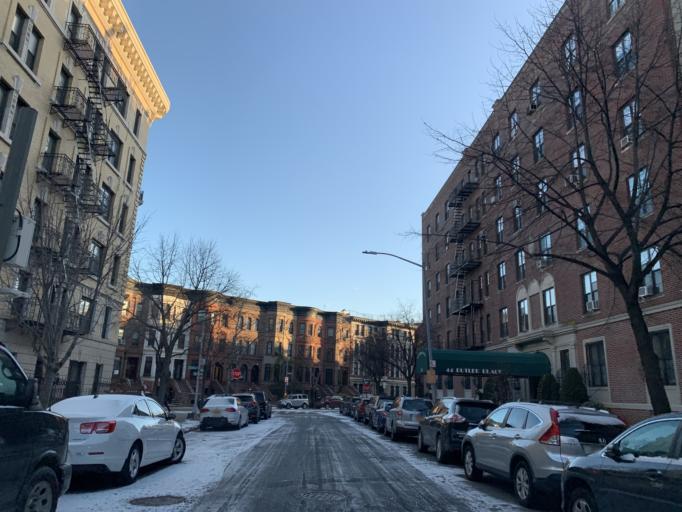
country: US
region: New York
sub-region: Kings County
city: Brooklyn
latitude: 40.6752
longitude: -73.9681
